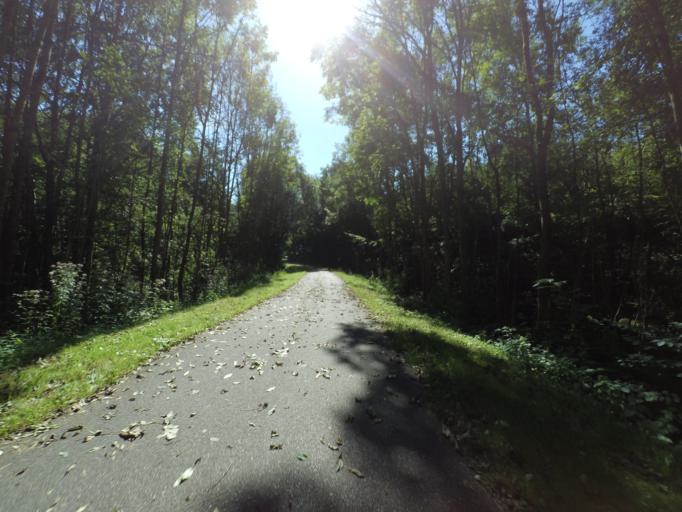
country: DE
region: Rheinland-Pfalz
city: Niederofflingen
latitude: 50.0720
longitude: 6.8823
